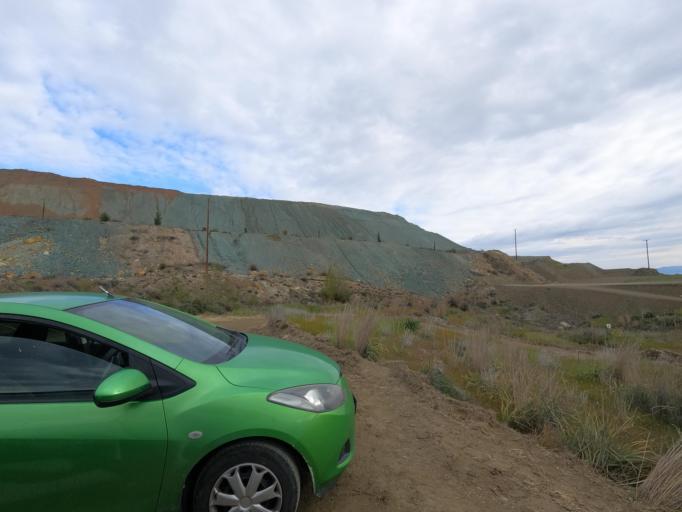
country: CY
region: Lefkosia
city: Lefka
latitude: 35.0849
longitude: 32.9002
